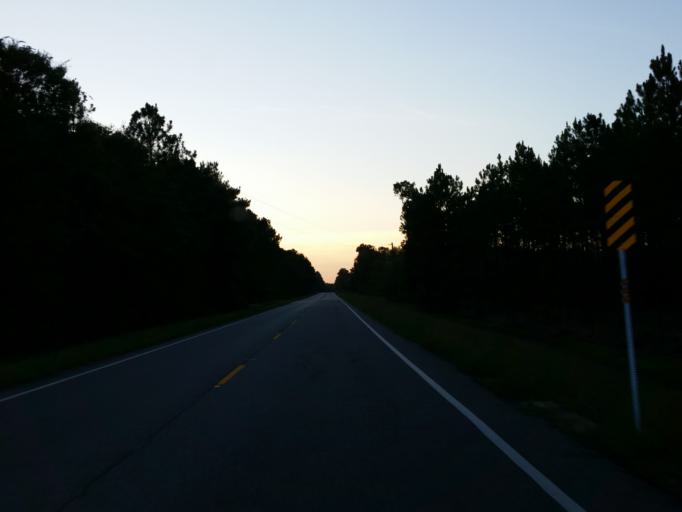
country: US
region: Georgia
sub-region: Berrien County
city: Nashville
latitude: 31.2264
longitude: -83.2977
